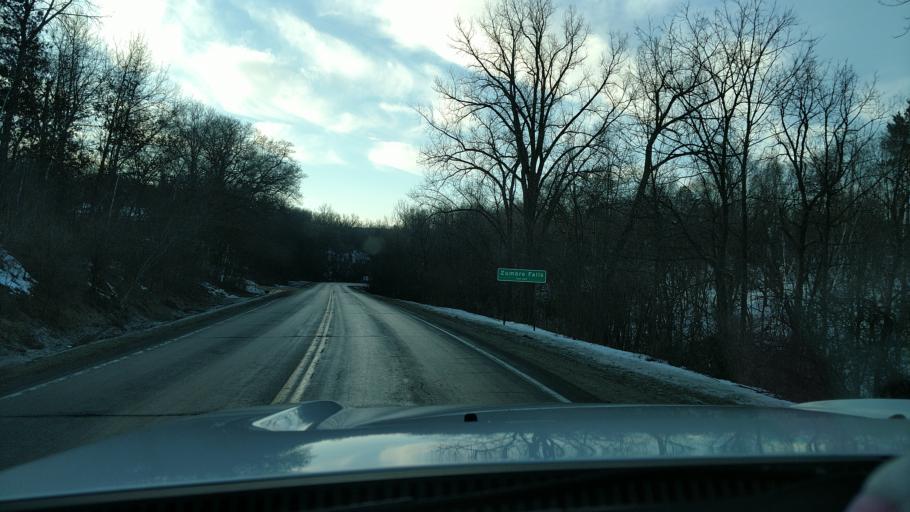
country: US
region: Minnesota
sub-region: Olmsted County
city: Oronoco
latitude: 44.2876
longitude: -92.4213
